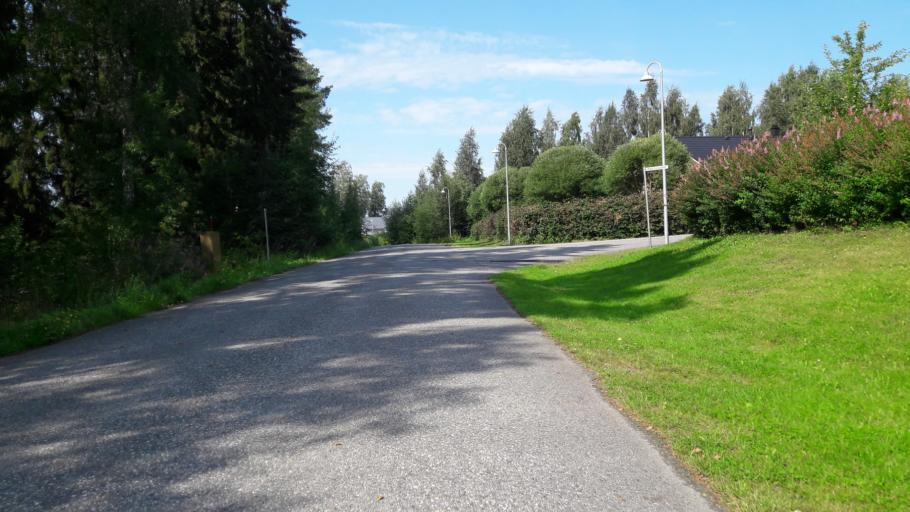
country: FI
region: North Karelia
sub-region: Joensuu
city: Joensuu
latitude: 62.5258
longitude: 29.8406
